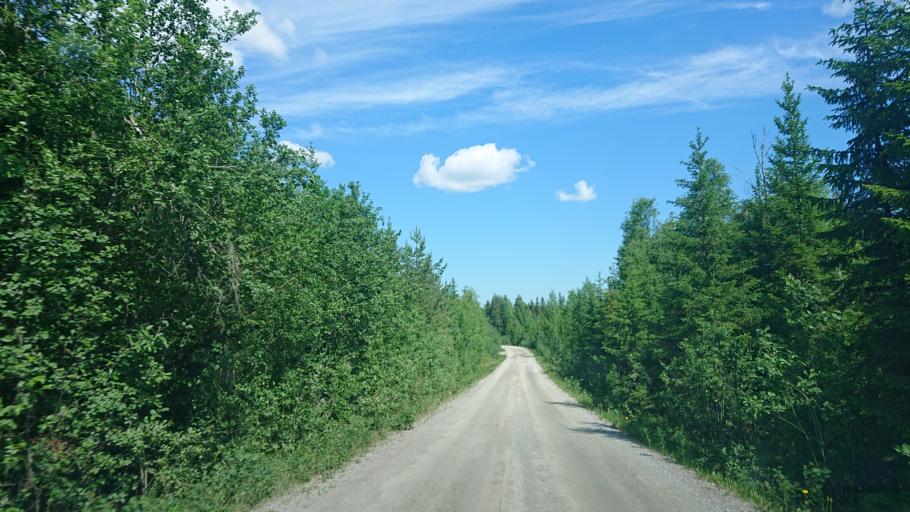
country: SE
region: Vaesternorrland
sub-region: Solleftea Kommun
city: Solleftea
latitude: 62.9461
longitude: 17.1315
